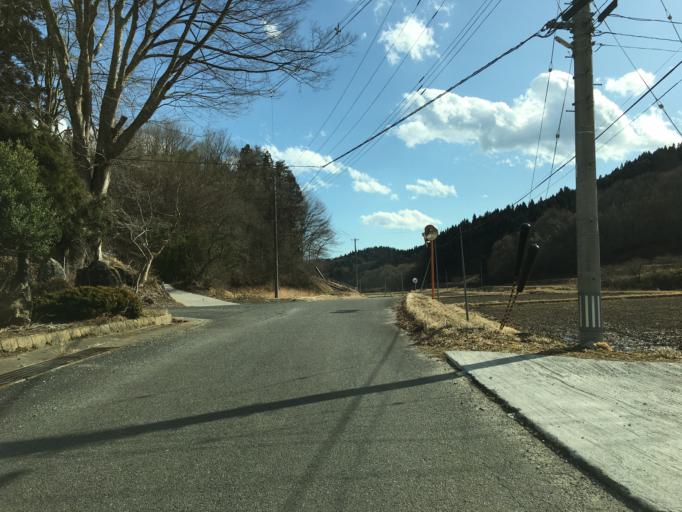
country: JP
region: Fukushima
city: Ishikawa
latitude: 37.2332
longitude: 140.5925
